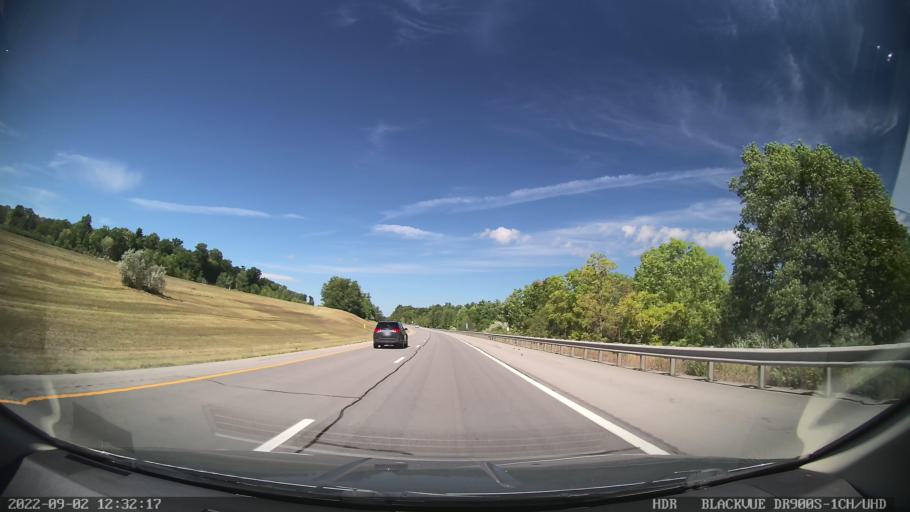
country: US
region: New York
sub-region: Livingston County
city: Dansville
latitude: 42.6207
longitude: -77.7708
